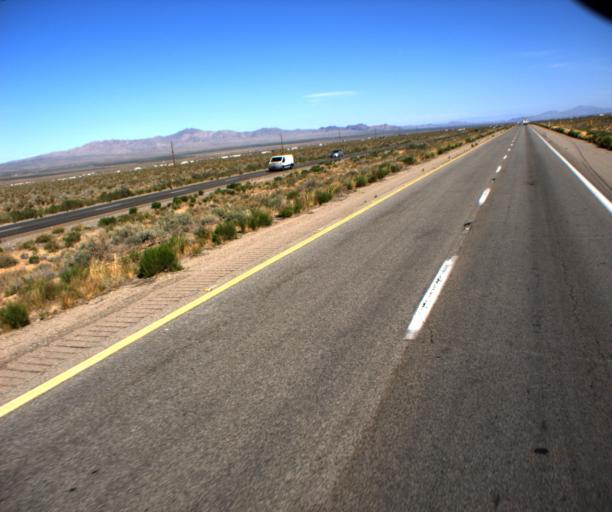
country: US
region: Arizona
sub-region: Mohave County
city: Dolan Springs
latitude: 35.4799
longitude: -114.3178
